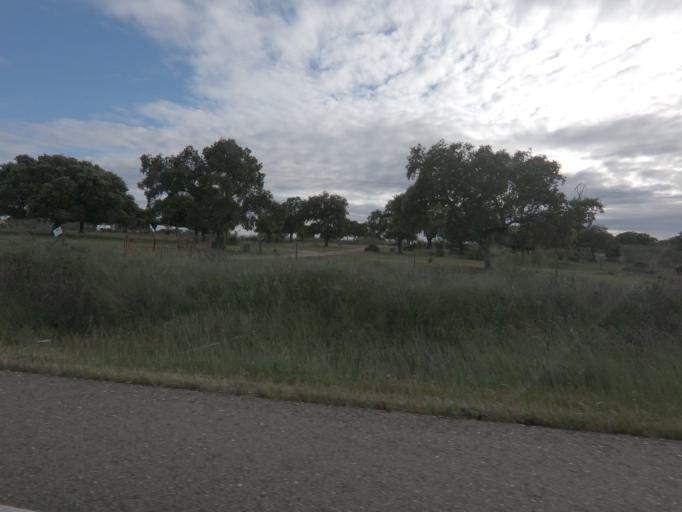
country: ES
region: Extremadura
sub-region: Provincia de Caceres
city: Torrejoncillo
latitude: 39.9151
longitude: -6.4865
